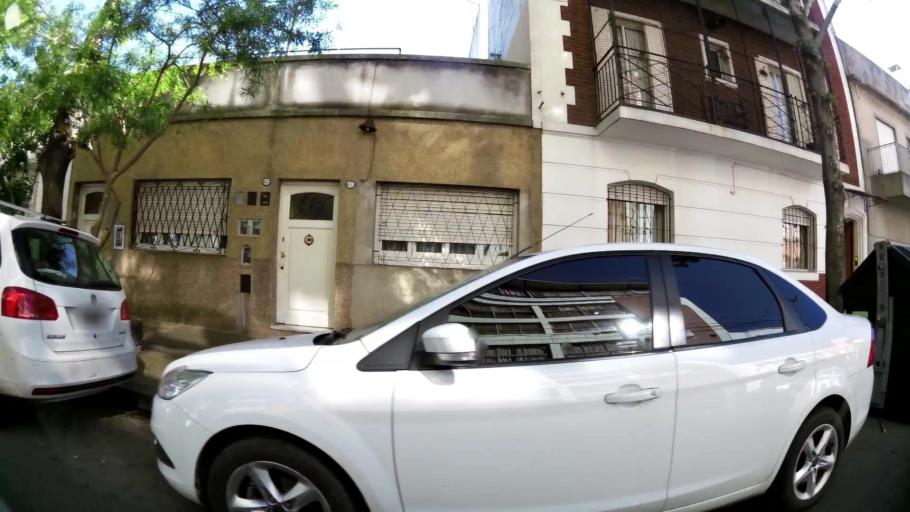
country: AR
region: Buenos Aires F.D.
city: Colegiales
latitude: -34.5528
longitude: -58.4854
